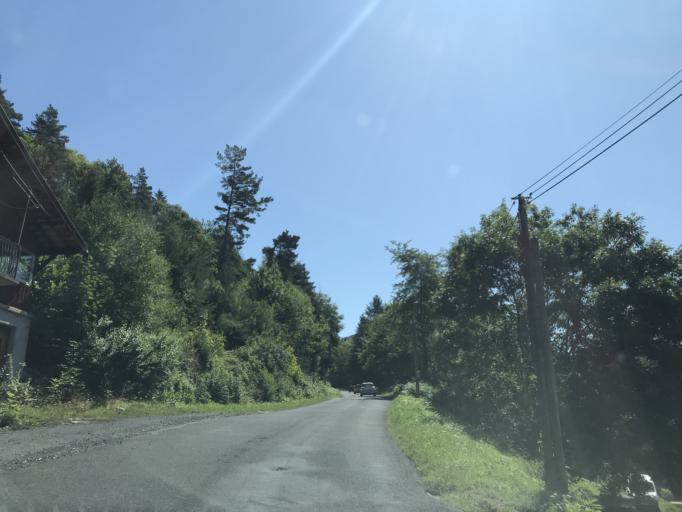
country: FR
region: Auvergne
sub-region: Departement du Puy-de-Dome
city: Job
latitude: 45.6709
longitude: 3.7332
